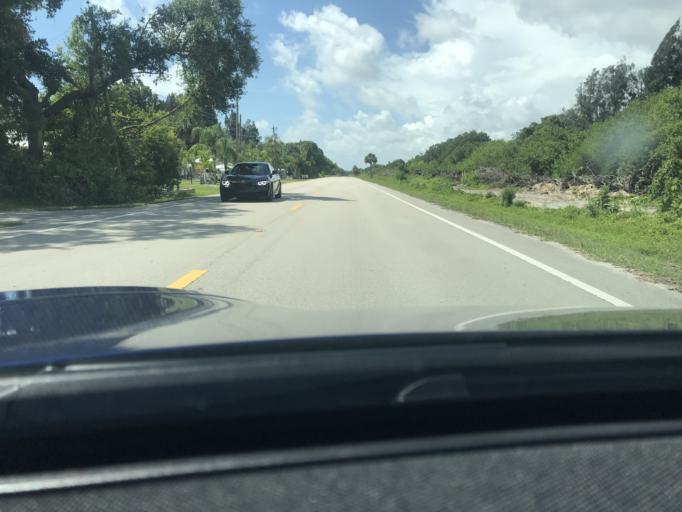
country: US
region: Florida
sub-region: Indian River County
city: Winter Beach
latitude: 27.7390
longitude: -80.4321
